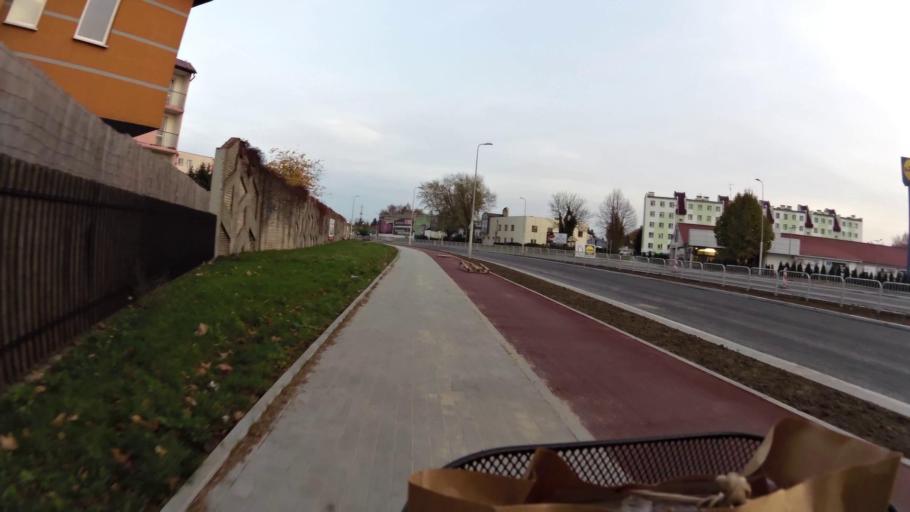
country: PL
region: West Pomeranian Voivodeship
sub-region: Koszalin
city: Koszalin
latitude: 54.1838
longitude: 16.1796
